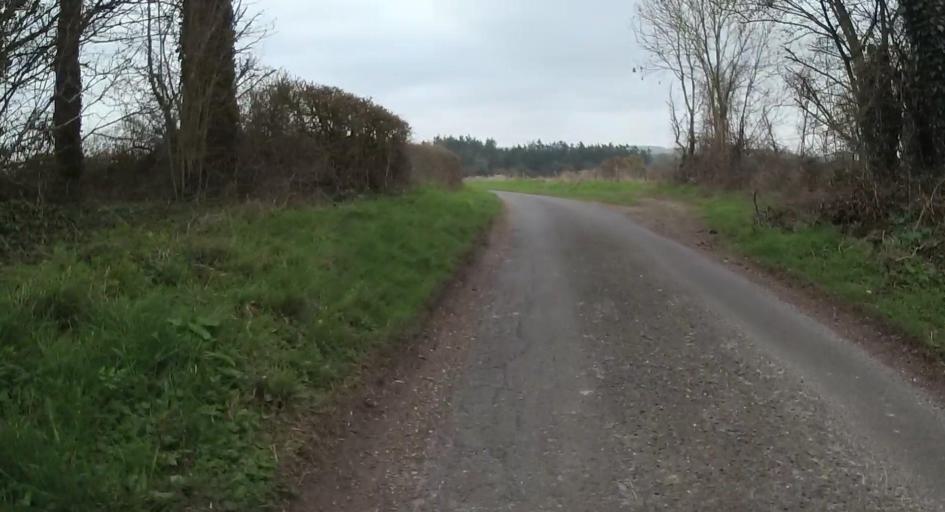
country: GB
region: England
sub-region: Hampshire
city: Four Marks
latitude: 51.1128
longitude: -1.1350
